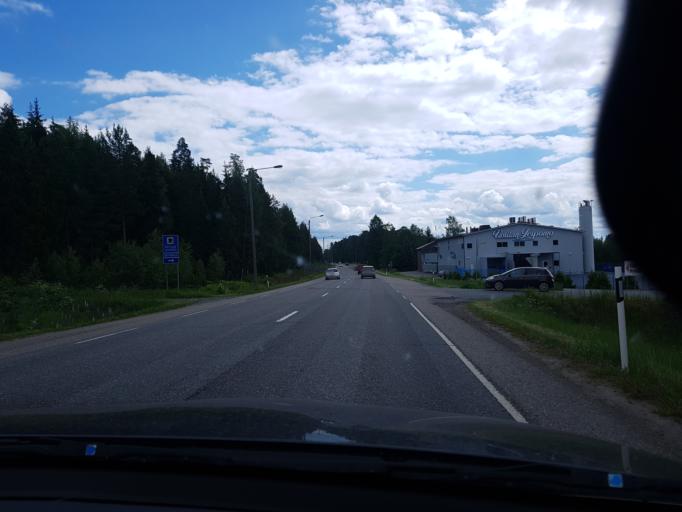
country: FI
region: Pirkanmaa
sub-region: Tampere
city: Paelkaene
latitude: 61.3026
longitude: 24.3009
